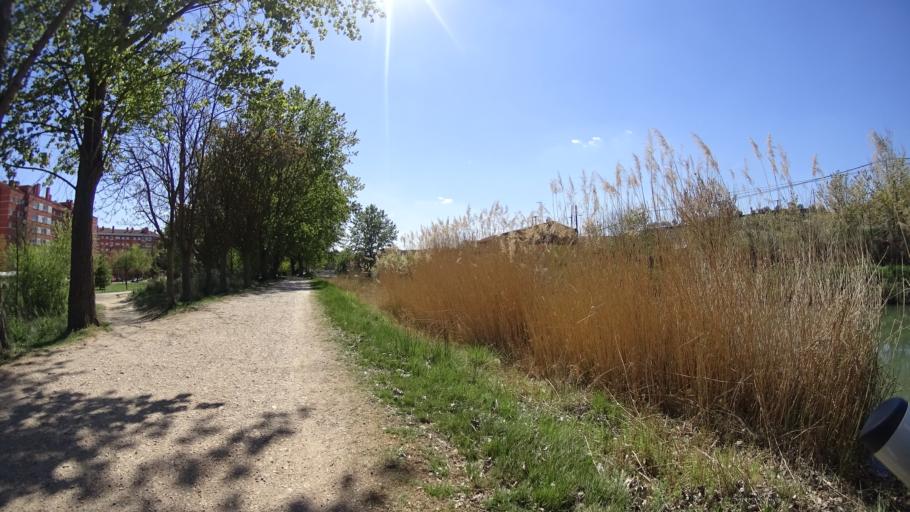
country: ES
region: Castille and Leon
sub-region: Provincia de Valladolid
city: Valladolid
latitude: 41.6735
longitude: -4.7304
